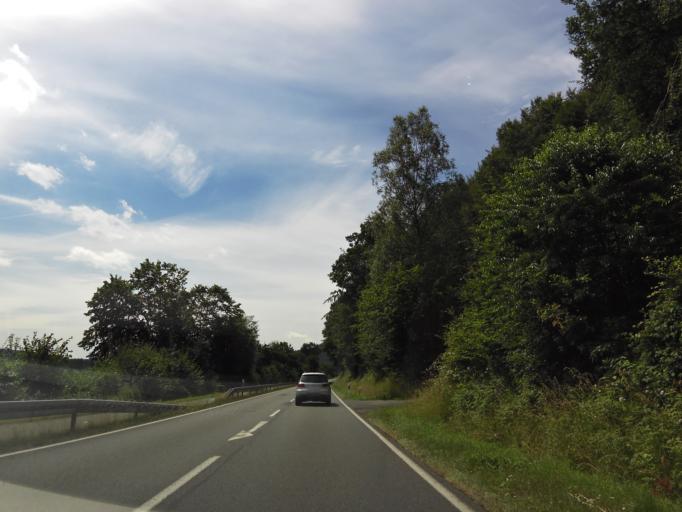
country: DE
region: Lower Saxony
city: Bad Karlshafen
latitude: 51.6493
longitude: 9.4941
